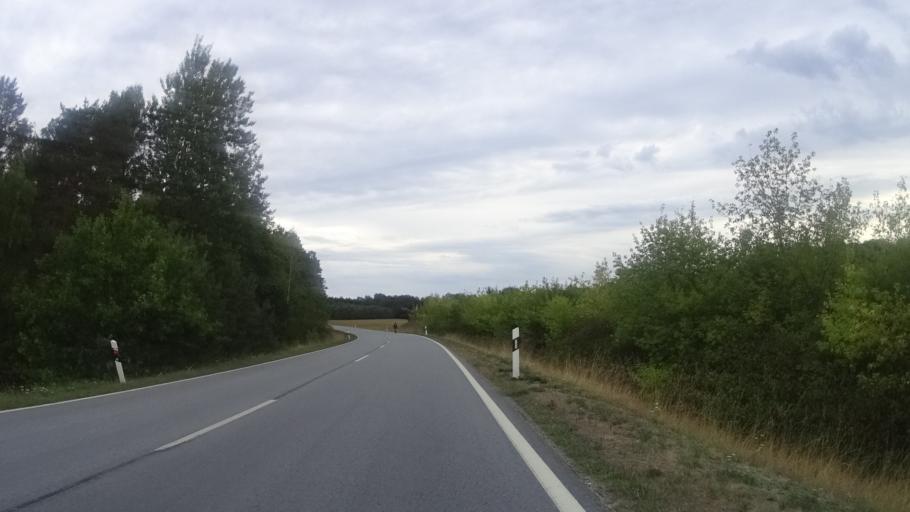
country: PL
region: Lower Silesian Voivodeship
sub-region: Powiat zgorzelecki
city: Piensk
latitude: 51.2872
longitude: 15.0239
